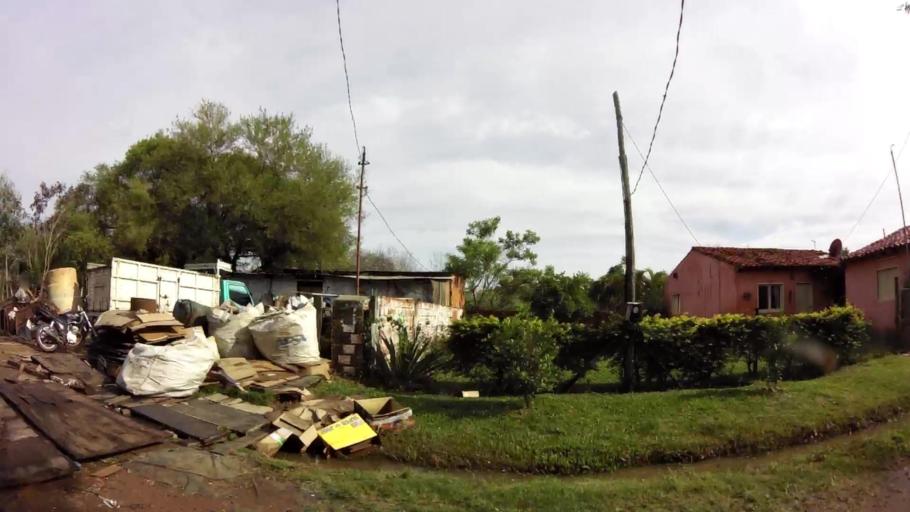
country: PY
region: Central
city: Limpio
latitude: -25.1721
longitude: -57.4940
